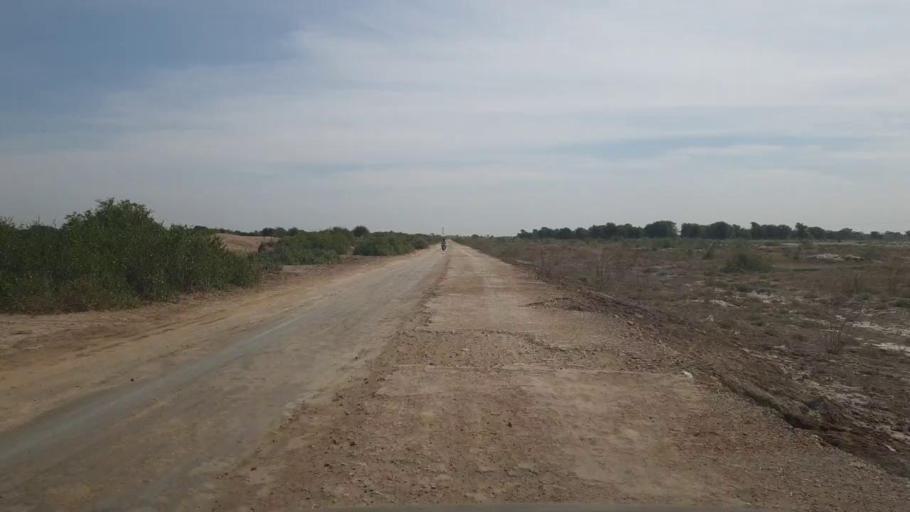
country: PK
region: Sindh
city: Kunri
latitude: 25.2974
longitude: 69.5786
